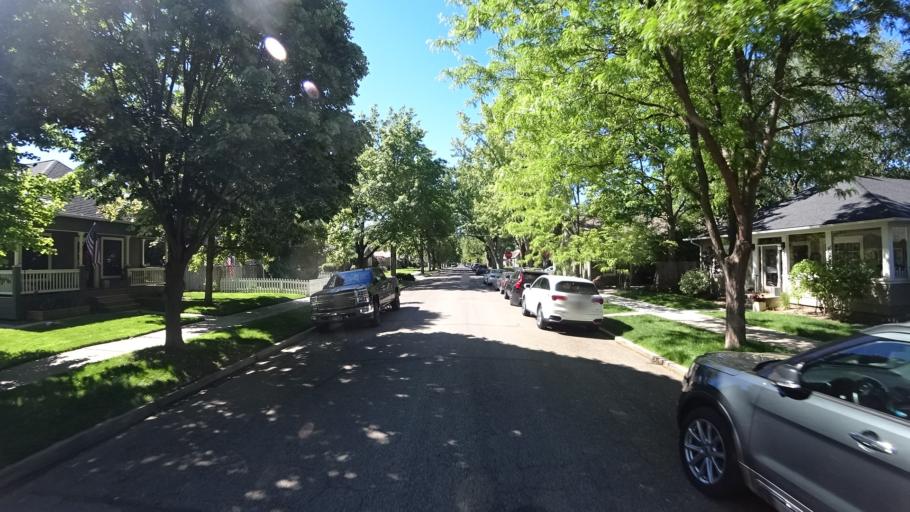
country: US
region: Idaho
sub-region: Ada County
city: Boise
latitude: 43.6325
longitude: -116.2134
